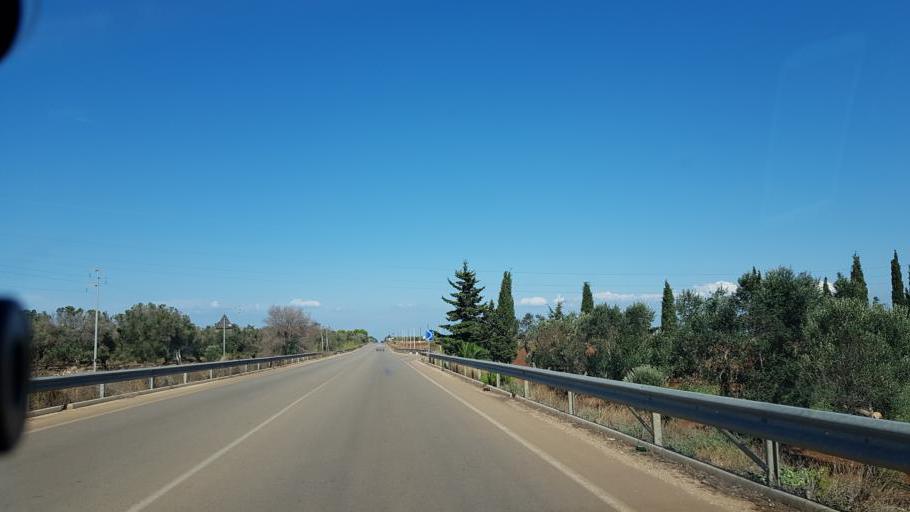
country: IT
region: Apulia
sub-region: Provincia di Lecce
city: Leverano
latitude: 40.2435
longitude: 17.9733
